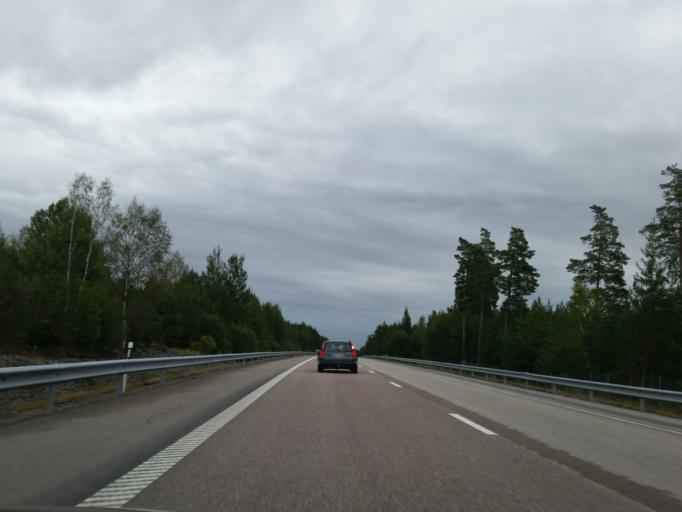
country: SE
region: Uppsala
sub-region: Enkopings Kommun
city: Grillby
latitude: 59.6313
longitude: 17.3219
